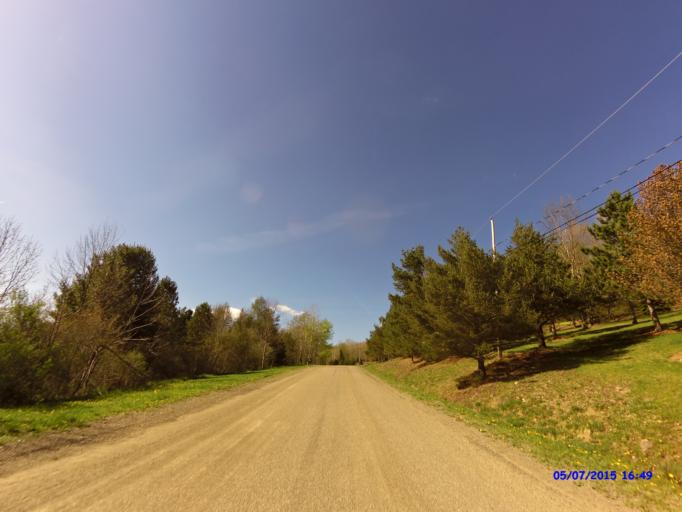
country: US
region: New York
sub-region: Cattaraugus County
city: Little Valley
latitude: 42.2818
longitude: -78.6989
